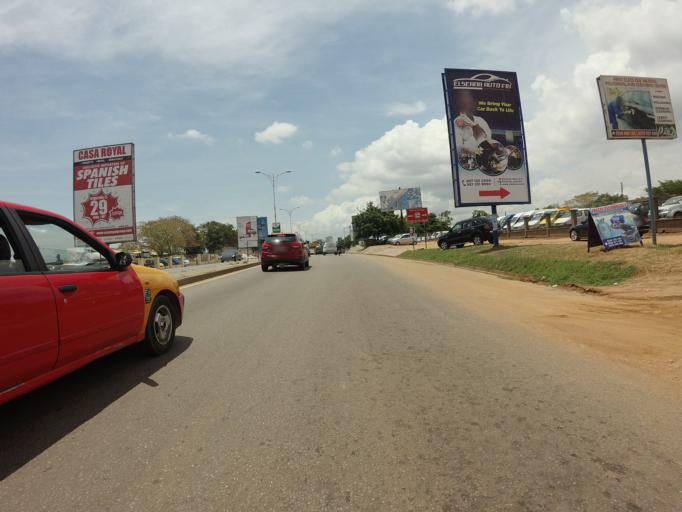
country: GH
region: Greater Accra
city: Medina Estates
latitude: 5.6264
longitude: -0.1565
